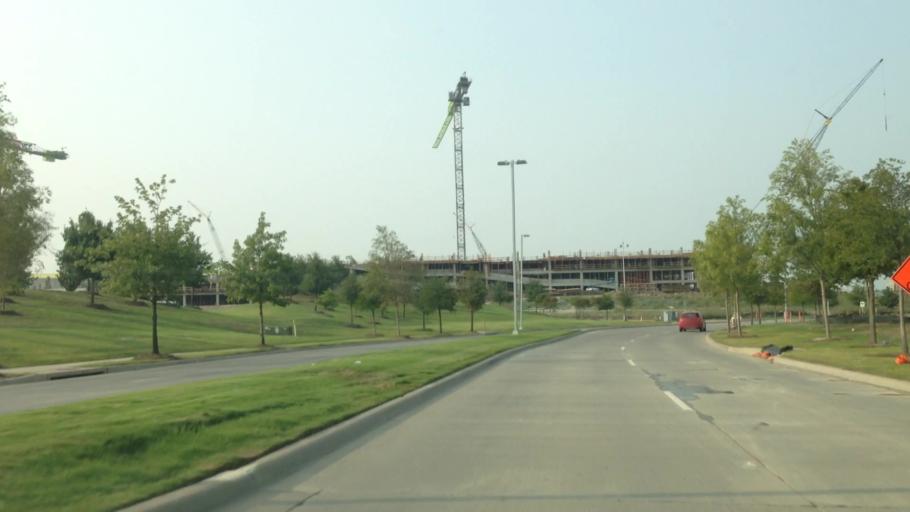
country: US
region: Texas
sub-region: Denton County
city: The Colony
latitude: 33.0698
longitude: -96.8600
